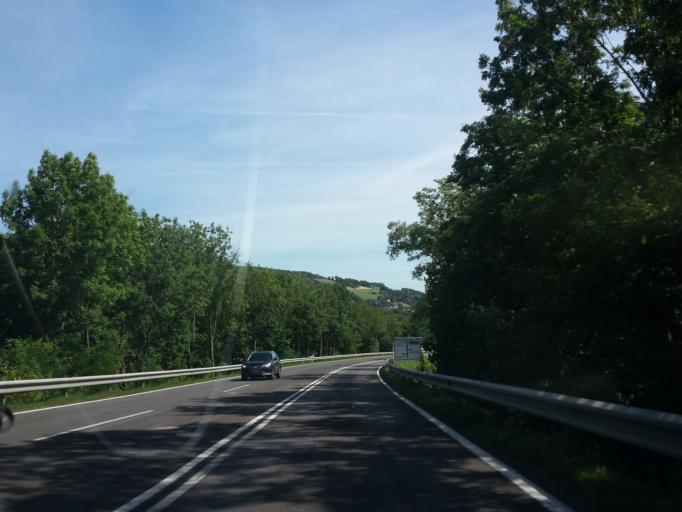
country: AT
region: Lower Austria
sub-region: Politischer Bezirk Neunkirchen
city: Enzenreith
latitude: 47.6708
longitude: 15.9508
